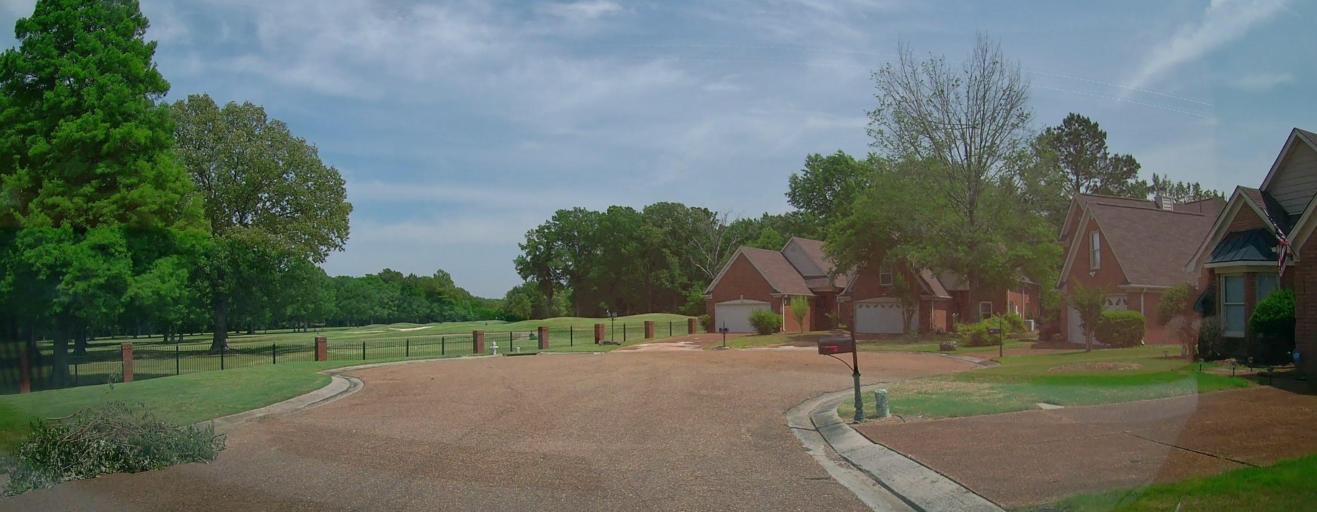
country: US
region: Tennessee
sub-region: Shelby County
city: Germantown
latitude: 35.0379
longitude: -89.7839
